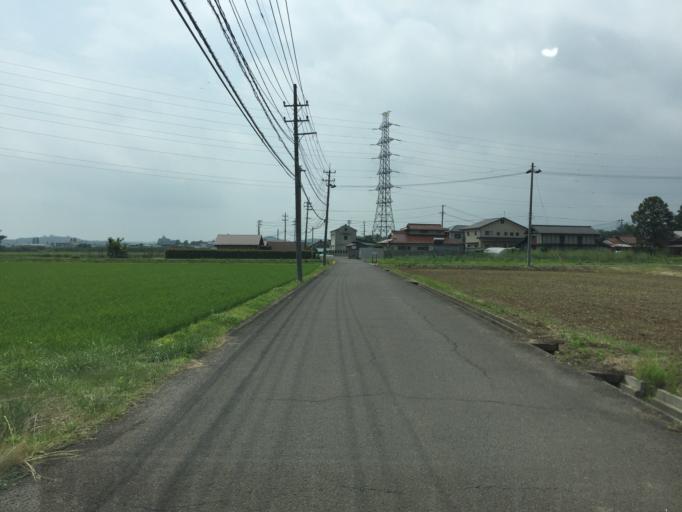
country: JP
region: Fukushima
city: Fukushima-shi
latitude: 37.7481
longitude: 140.4158
